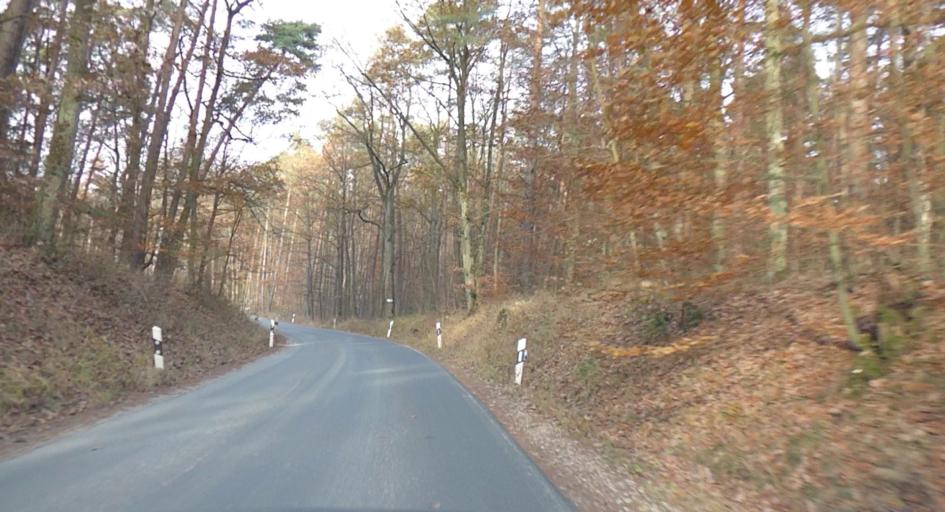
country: DE
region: Bavaria
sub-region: Regierungsbezirk Mittelfranken
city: Bubenreuth
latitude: 49.6123
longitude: 11.0239
